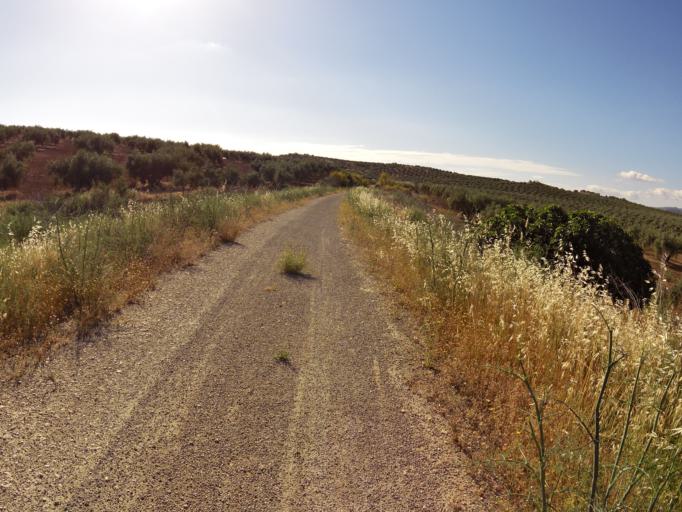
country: ES
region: Andalusia
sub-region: Province of Cordoba
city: Luque
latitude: 37.5833
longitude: -4.1993
